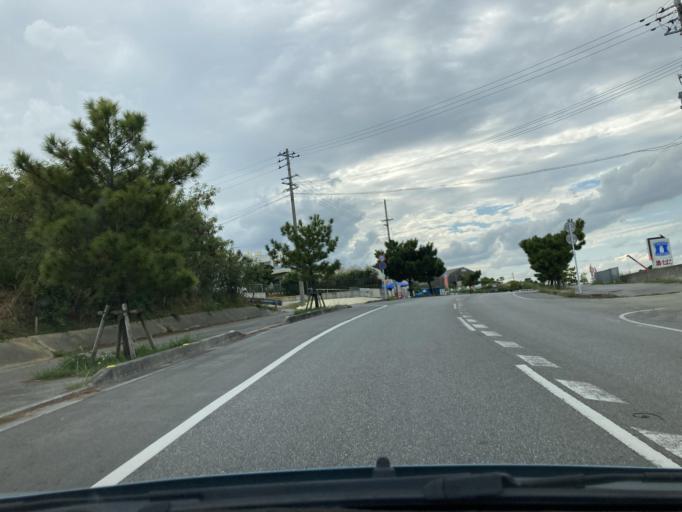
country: JP
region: Okinawa
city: Katsuren-haebaru
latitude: 26.3284
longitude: 127.8929
